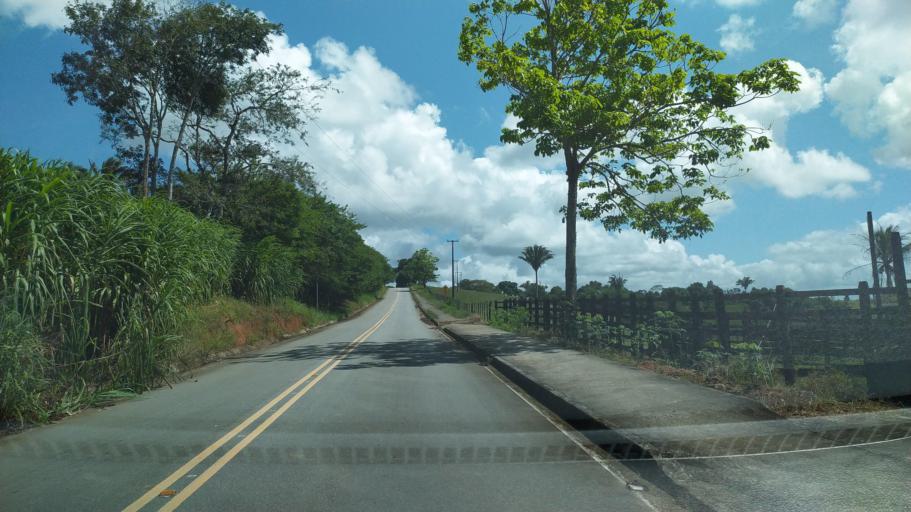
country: BR
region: Alagoas
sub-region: Uniao Dos Palmares
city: Uniao dos Palmares
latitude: -9.1625
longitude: -36.0689
